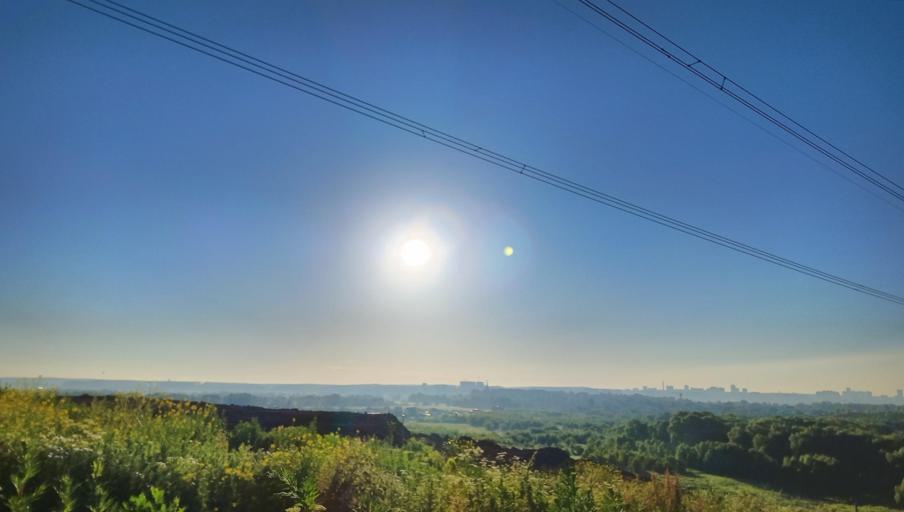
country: RU
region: Moskovskaya
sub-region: Leninskiy Rayon
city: Molokovo
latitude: 55.5847
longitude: 37.8215
